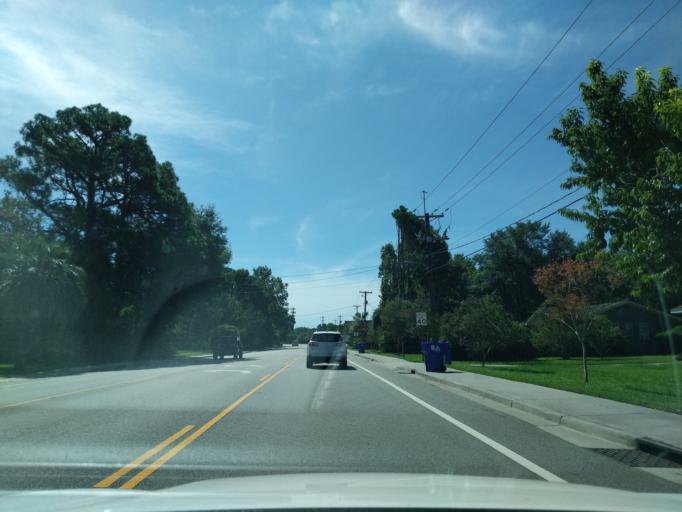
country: US
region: South Carolina
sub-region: Charleston County
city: Charleston
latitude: 32.7438
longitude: -79.9394
